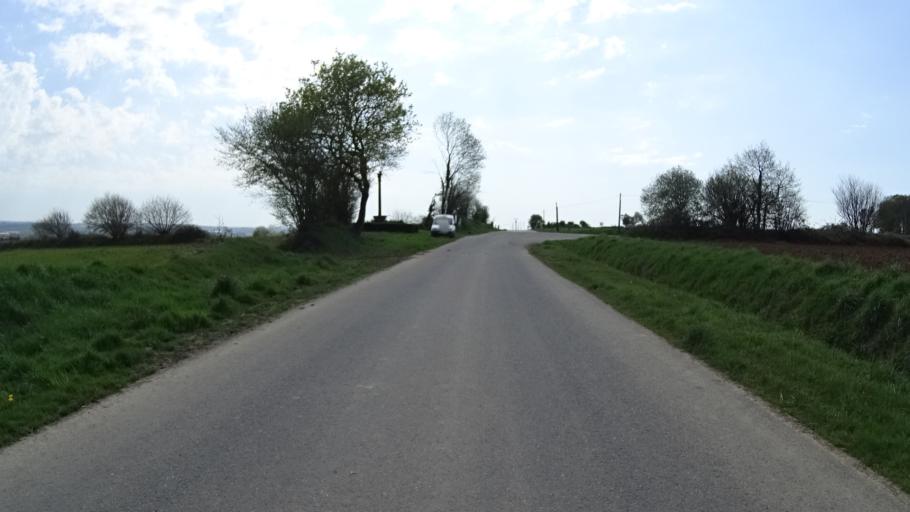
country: FR
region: Brittany
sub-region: Departement du Finistere
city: Sizun
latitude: 48.4390
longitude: -4.1169
